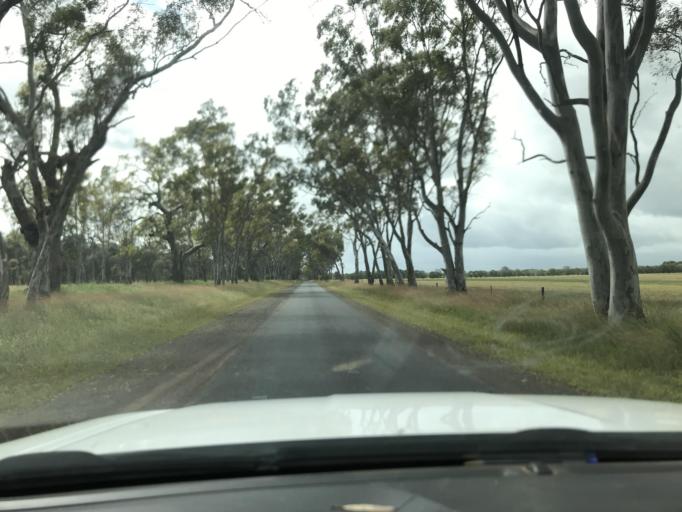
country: AU
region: South Australia
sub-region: Wattle Range
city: Penola
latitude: -37.1652
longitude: 141.4146
